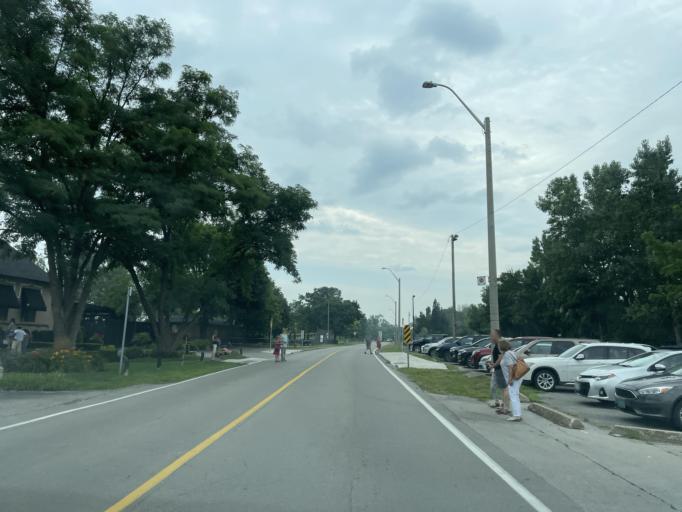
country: CA
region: Ontario
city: Hamilton
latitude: 43.2557
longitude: -79.7622
